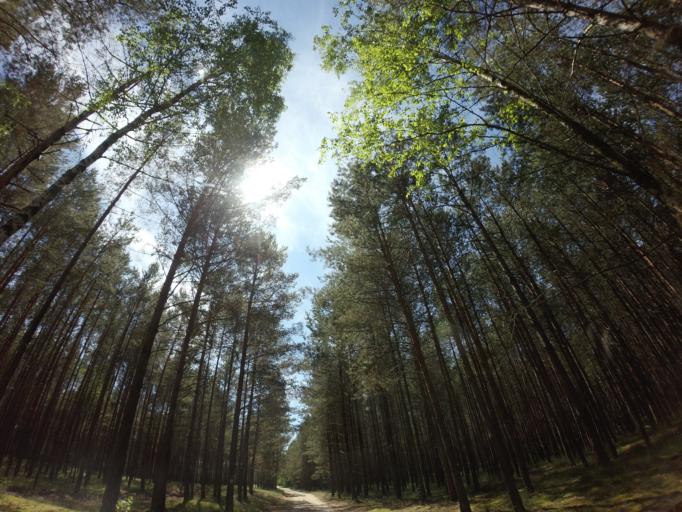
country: PL
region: West Pomeranian Voivodeship
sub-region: Powiat choszczenski
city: Drawno
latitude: 53.1253
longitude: 15.8300
